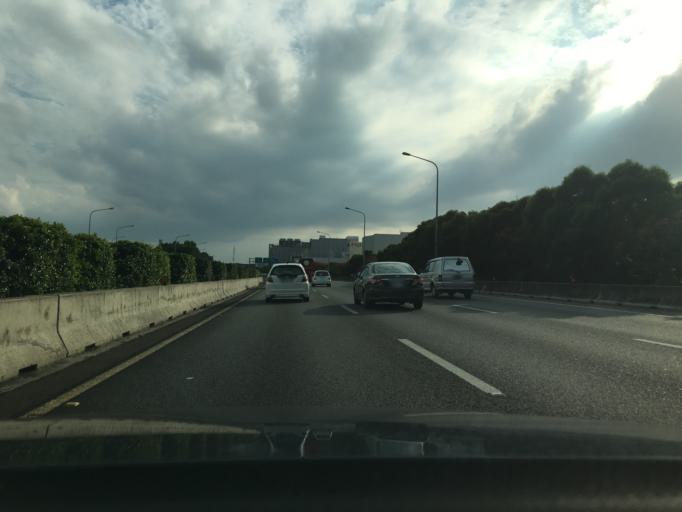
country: TW
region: Taiwan
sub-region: Hsinchu
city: Zhubei
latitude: 24.8660
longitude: 121.0134
